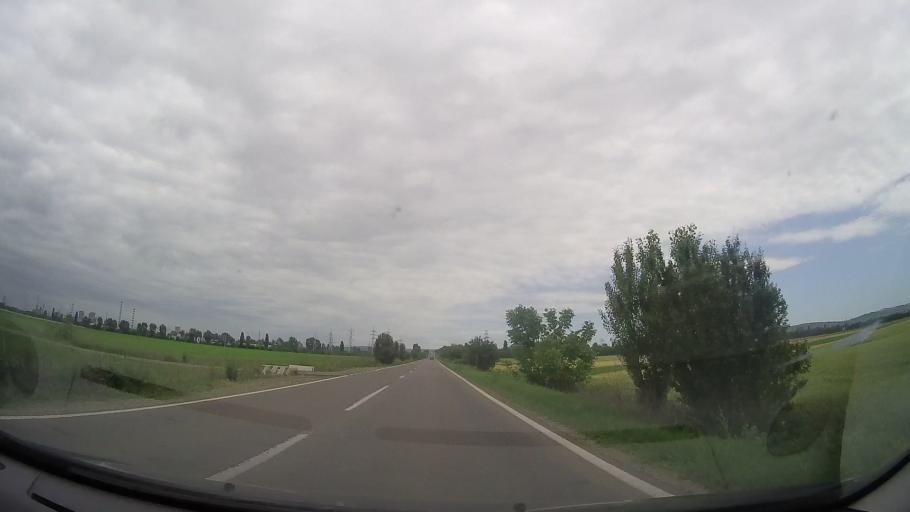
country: RO
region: Prahova
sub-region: Comuna Berceni
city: Berceni
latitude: 44.9342
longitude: 26.1038
